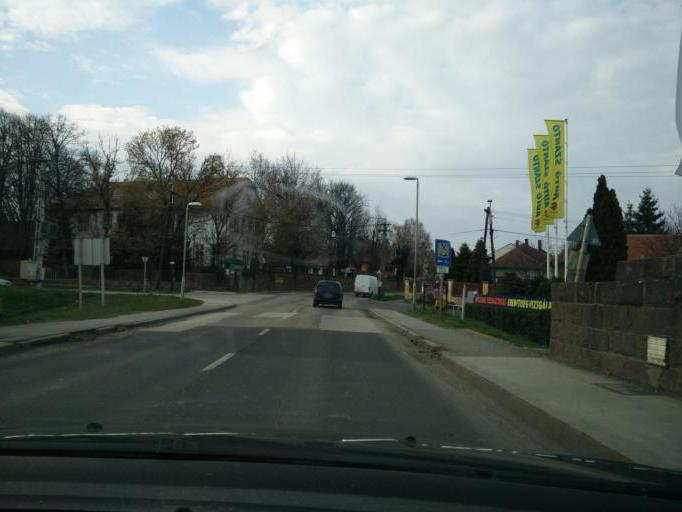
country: HU
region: Zala
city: Zalaegerszeg
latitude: 46.8508
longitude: 16.8453
